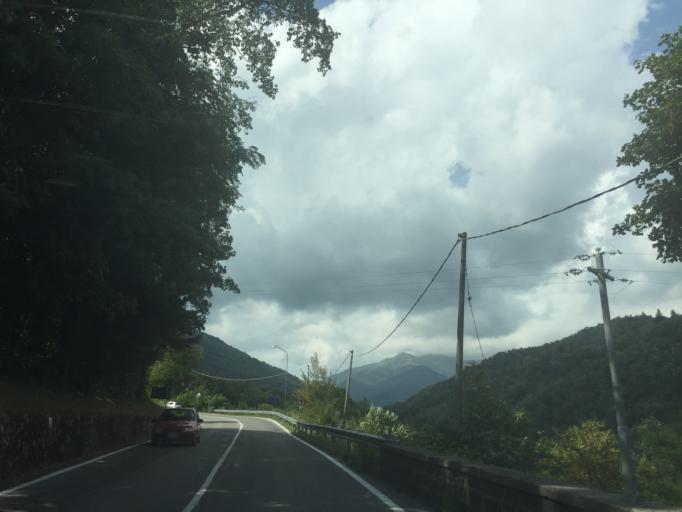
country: IT
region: Tuscany
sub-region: Provincia di Pistoia
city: Cutigliano
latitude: 44.0998
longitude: 10.7506
